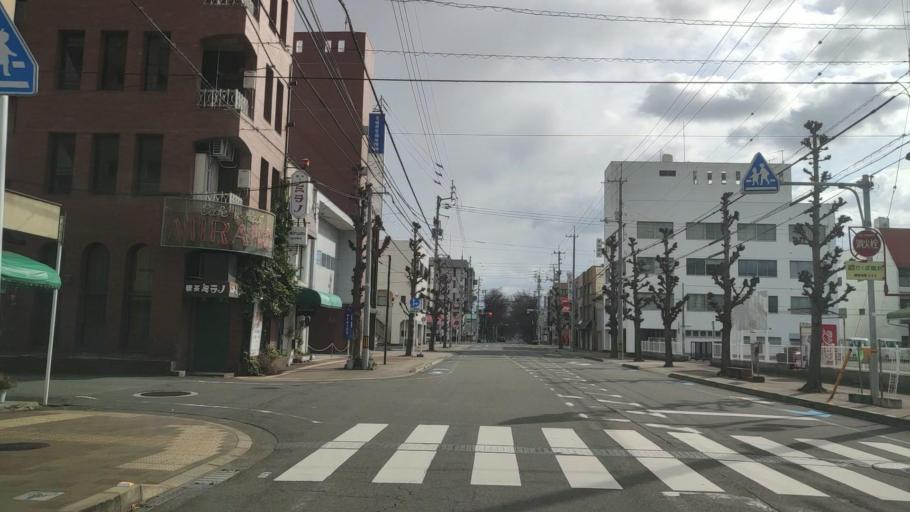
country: JP
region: Ehime
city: Hojo
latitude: 34.0639
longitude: 132.9956
